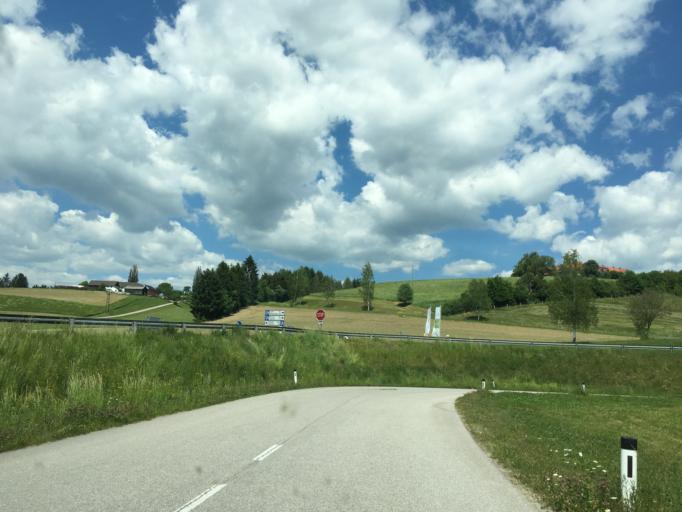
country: AT
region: Upper Austria
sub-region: Politischer Bezirk Perg
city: Perg
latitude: 48.3335
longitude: 14.5724
